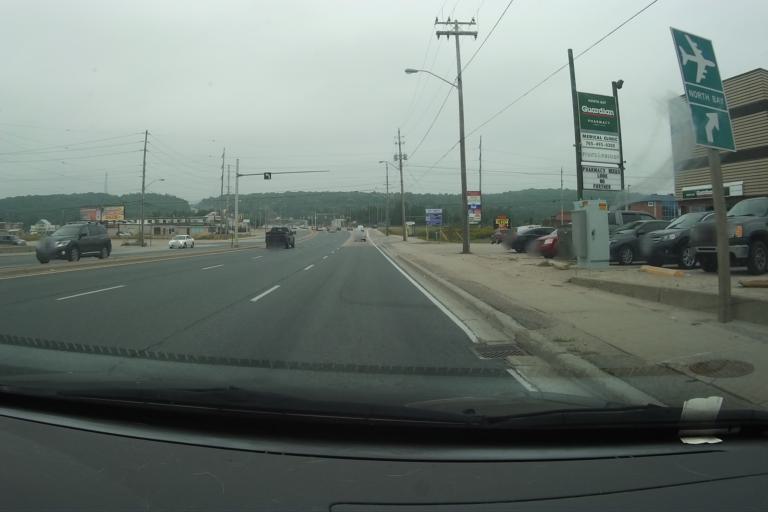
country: CA
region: Ontario
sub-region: Nipissing District
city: North Bay
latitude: 46.3319
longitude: -79.4660
